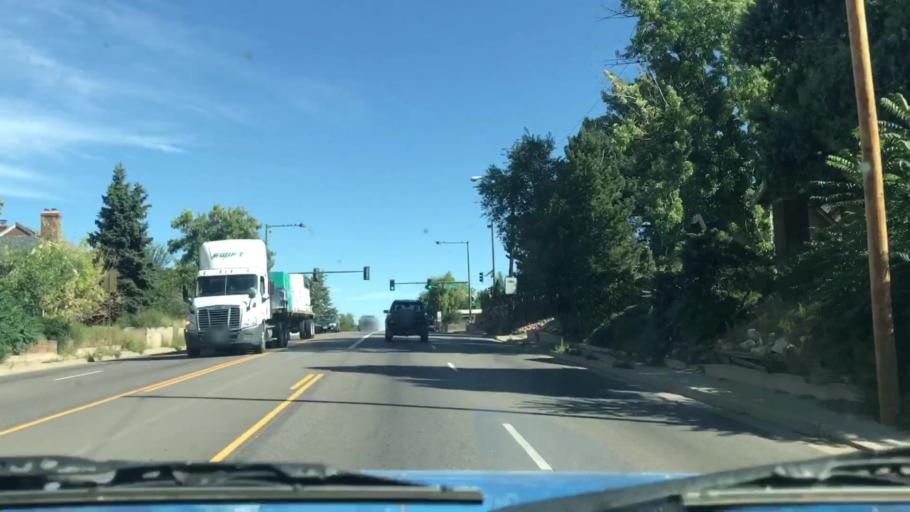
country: US
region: Colorado
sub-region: Jefferson County
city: Edgewater
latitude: 39.7608
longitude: -105.0532
